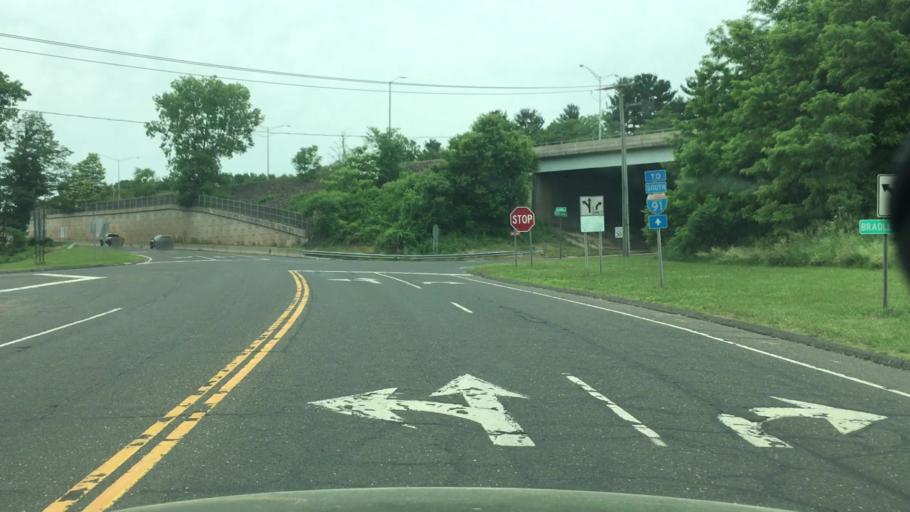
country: US
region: Connecticut
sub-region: Hartford County
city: Windsor Locks
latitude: 41.8944
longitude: -72.6413
